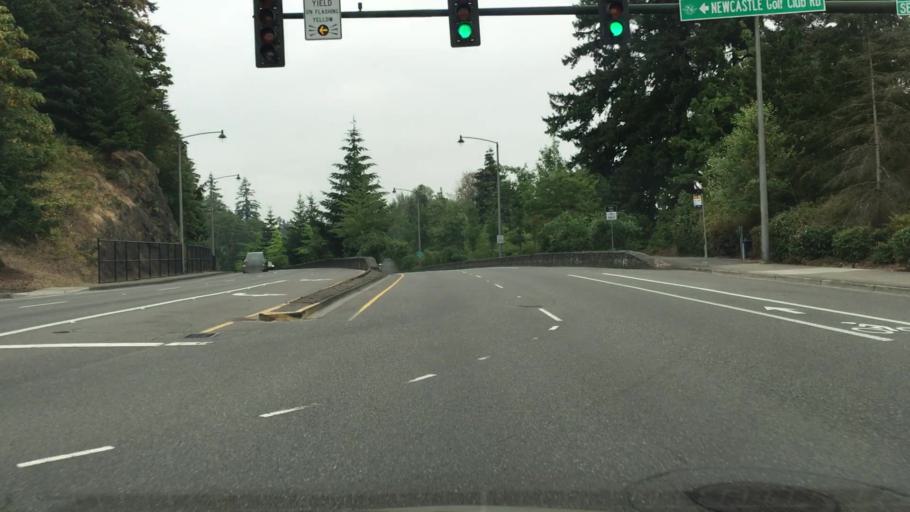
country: US
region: Washington
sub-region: King County
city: Newcastle
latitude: 47.5345
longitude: -122.1642
